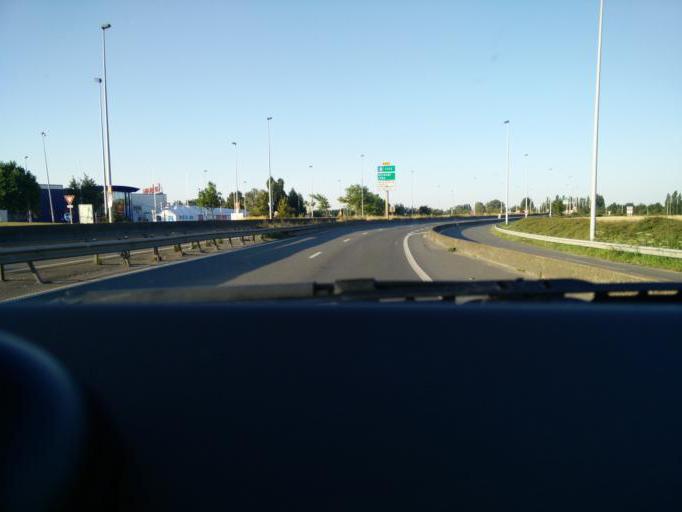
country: FR
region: Nord-Pas-de-Calais
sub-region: Departement du Nord
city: Capinghem
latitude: 50.6314
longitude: 2.9628
